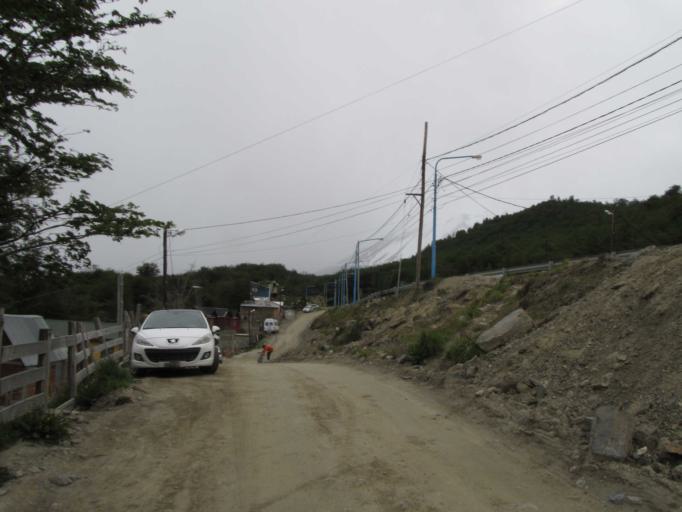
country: AR
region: Tierra del Fuego
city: Ushuaia
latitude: -54.7959
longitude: -68.2873
